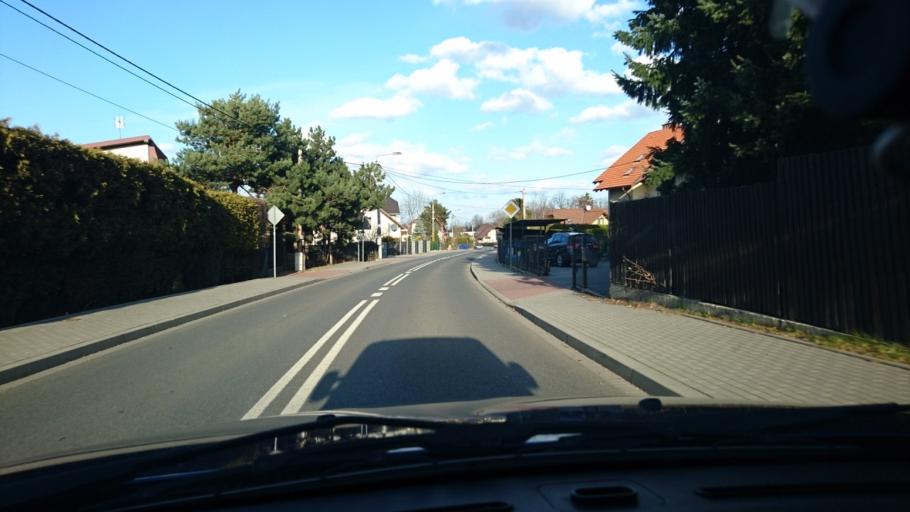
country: PL
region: Silesian Voivodeship
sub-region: Powiat bielski
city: Jaworze
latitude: 49.7920
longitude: 18.9829
